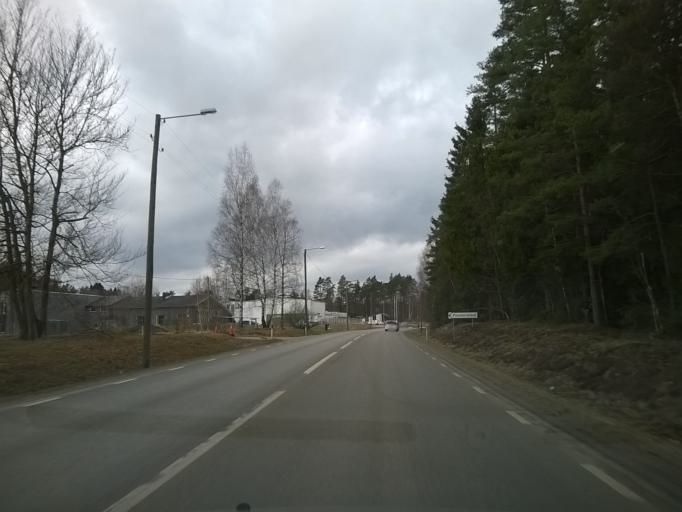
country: SE
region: Vaestra Goetaland
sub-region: Marks Kommun
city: Horred
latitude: 57.1431
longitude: 12.6931
